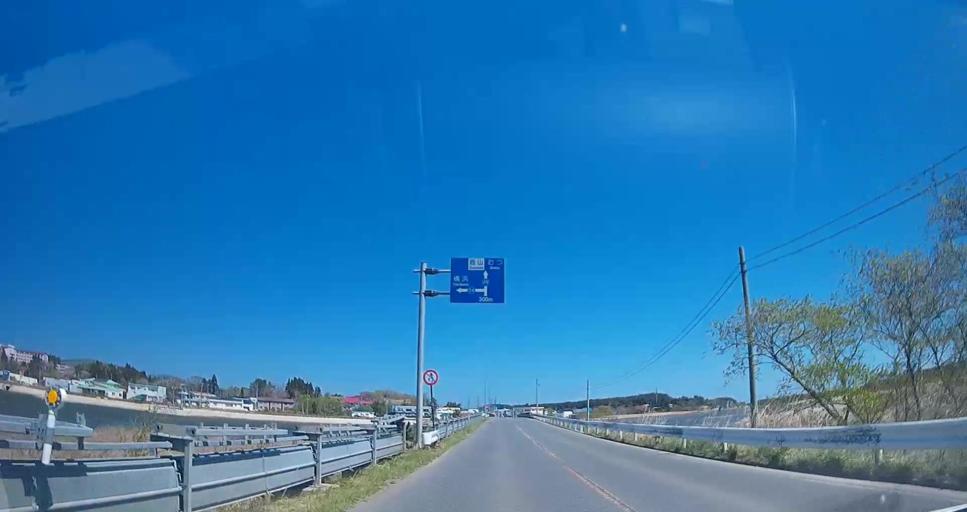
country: JP
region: Aomori
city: Misawa
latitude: 40.9578
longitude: 141.3711
